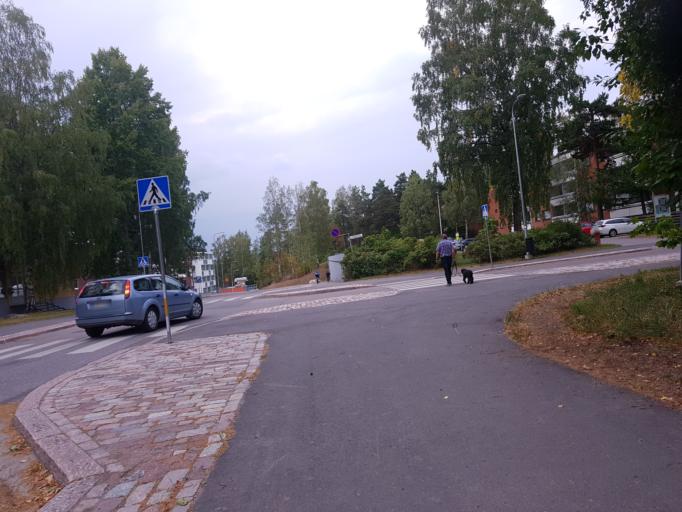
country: FI
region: Uusimaa
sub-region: Helsinki
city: Helsinki
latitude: 60.2326
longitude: 24.9500
